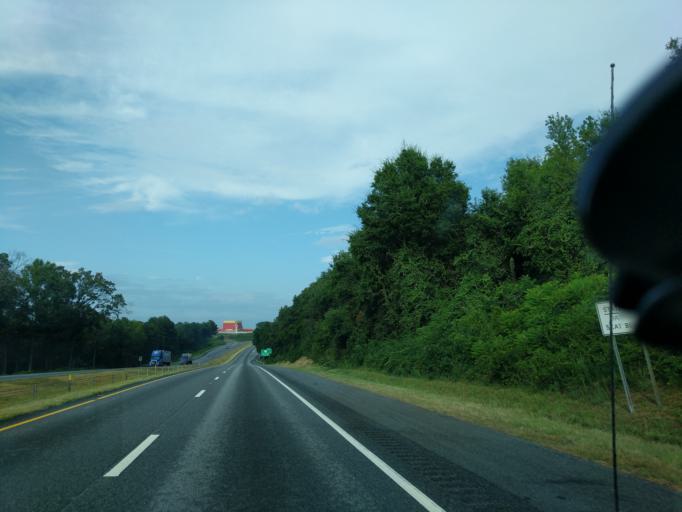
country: US
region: Georgia
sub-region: Hart County
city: Reed Creek
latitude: 34.4978
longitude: -83.0025
